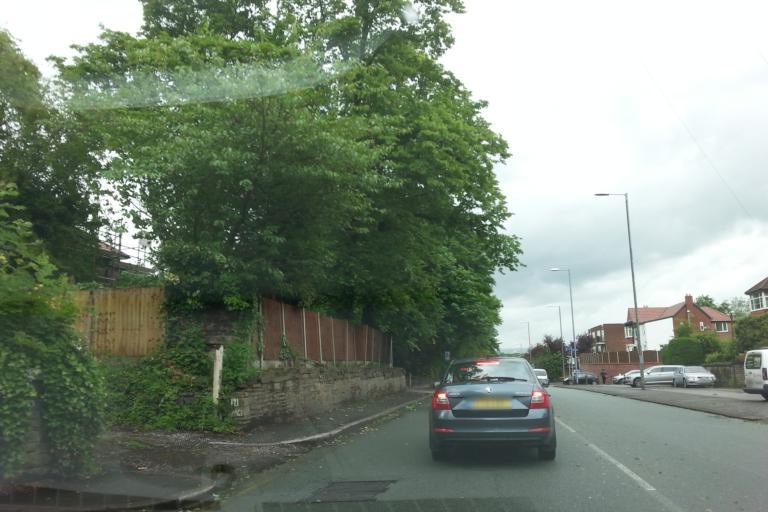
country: GB
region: England
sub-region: Manchester
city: Crumpsall
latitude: 53.5213
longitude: -2.2490
